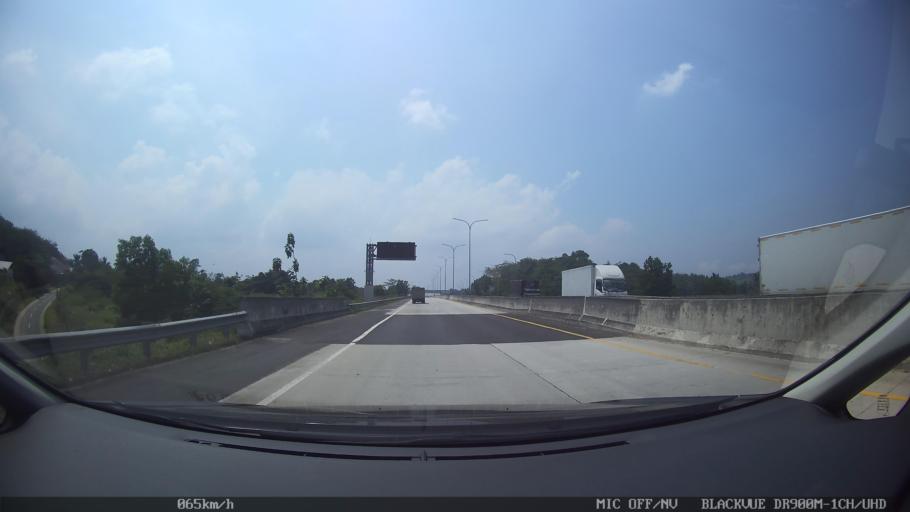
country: ID
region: Lampung
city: Kedaton
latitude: -5.3926
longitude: 105.3456
